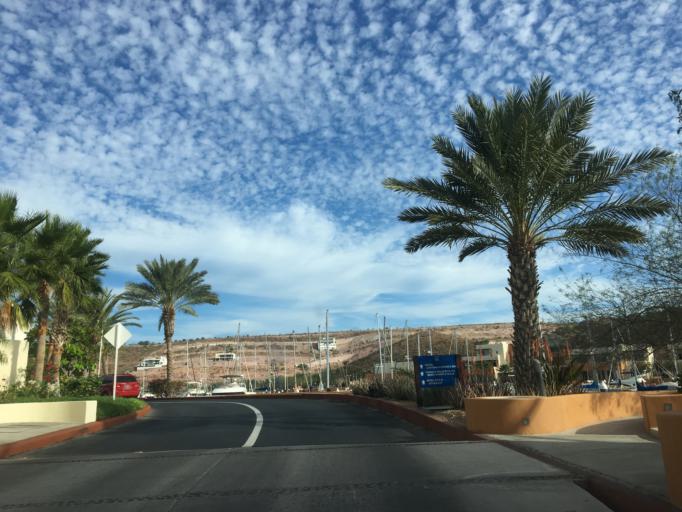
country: MX
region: Baja California Sur
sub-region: La Paz
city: La Paz
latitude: 24.2146
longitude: -110.2995
